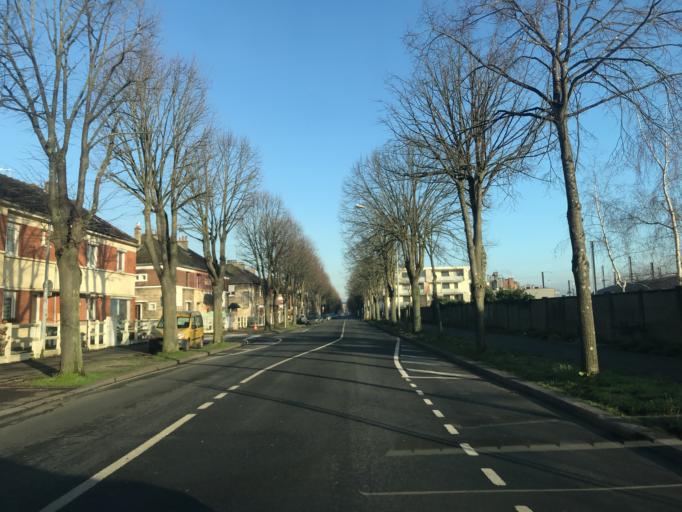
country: FR
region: Haute-Normandie
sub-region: Departement de la Seine-Maritime
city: Sotteville-les-Rouen
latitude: 49.4063
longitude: 1.1025
